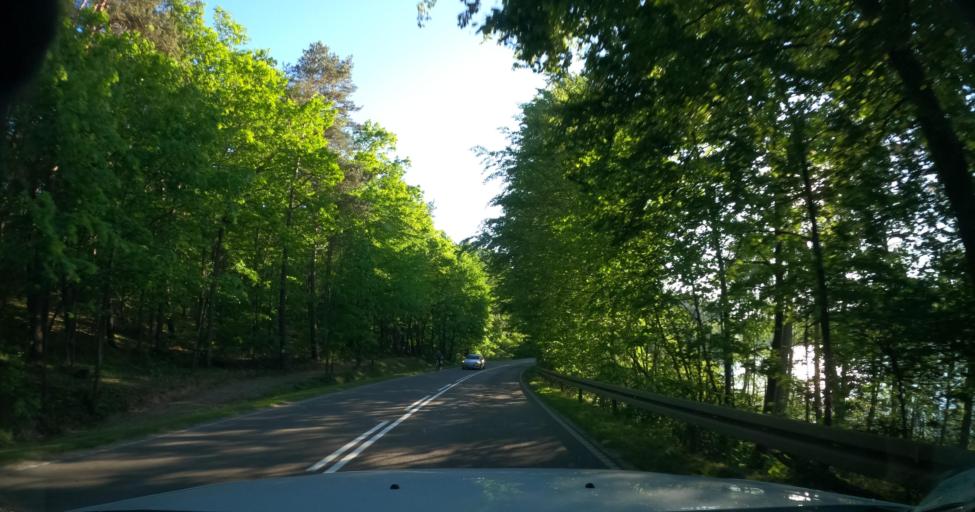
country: PL
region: Pomeranian Voivodeship
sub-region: Powiat kartuski
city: Zukowo
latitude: 54.3213
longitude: 18.3080
